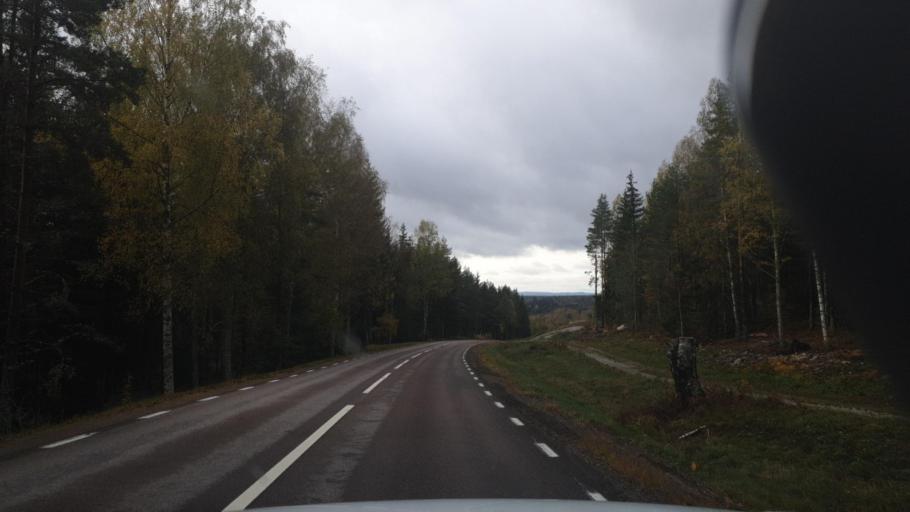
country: SE
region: Vaermland
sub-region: Sunne Kommun
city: Sunne
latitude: 59.6809
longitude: 13.0459
